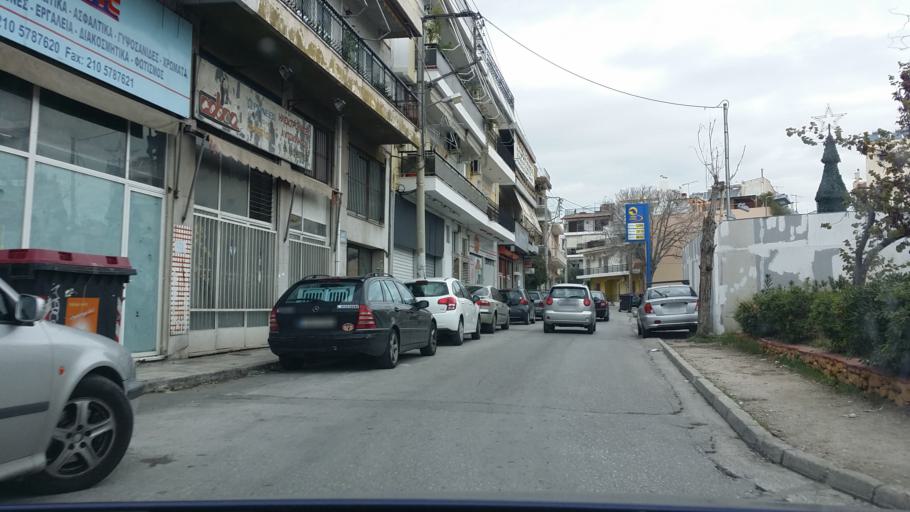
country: GR
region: Attica
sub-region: Nomarchia Athinas
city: Peristeri
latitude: 38.0224
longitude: 23.6942
